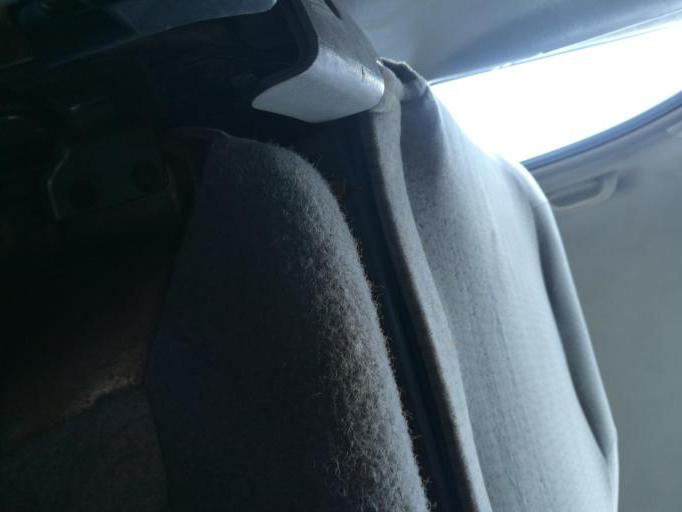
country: NG
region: Lagos
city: Lagos
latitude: 6.4629
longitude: 3.3811
